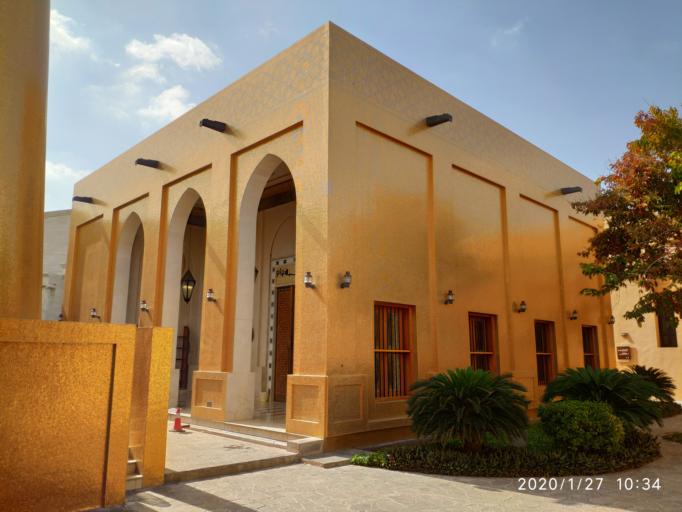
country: QA
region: Baladiyat ad Dawhah
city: Doha
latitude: 25.3611
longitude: 51.5268
